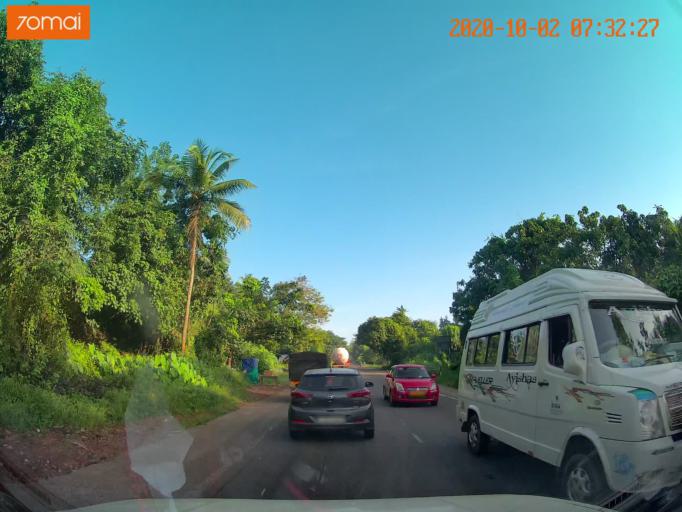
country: IN
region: Kerala
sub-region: Malappuram
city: Pariyapuram
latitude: 11.0537
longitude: 75.9361
